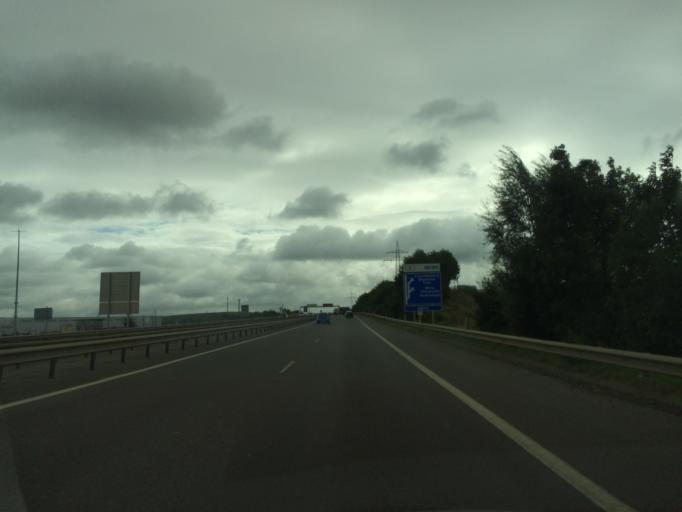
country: LU
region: Luxembourg
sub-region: Canton d'Esch-sur-Alzette
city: Dudelange
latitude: 49.4979
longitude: 6.0979
